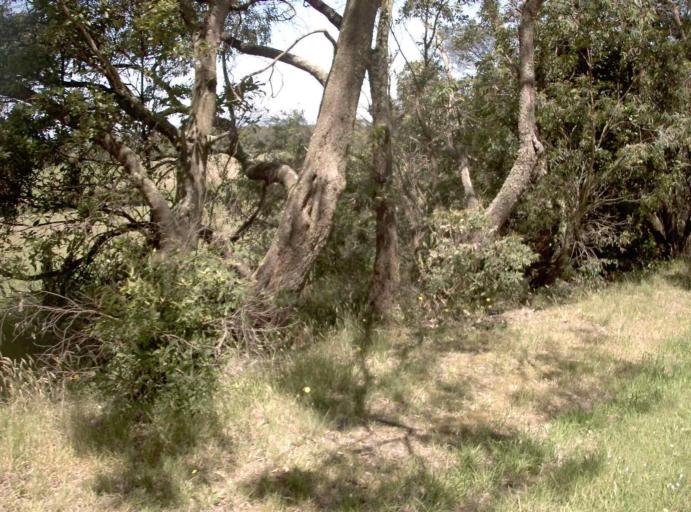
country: AU
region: Victoria
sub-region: Bass Coast
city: North Wonthaggi
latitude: -38.7696
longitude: 146.0648
